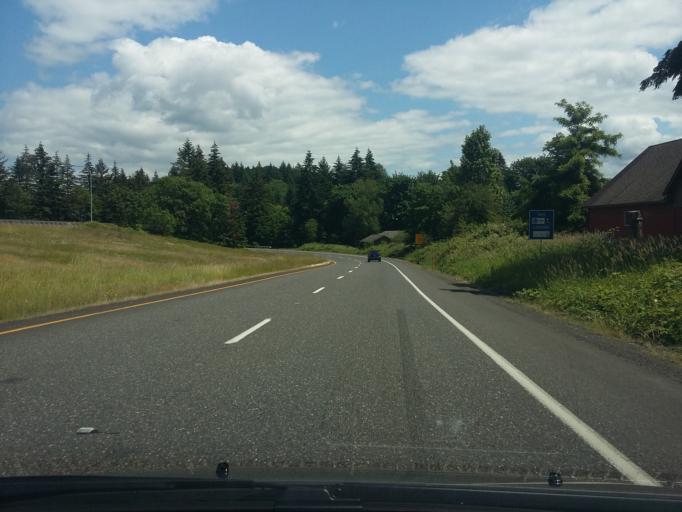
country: US
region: Washington
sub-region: Clark County
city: Camas
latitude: 45.5804
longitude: -122.4328
